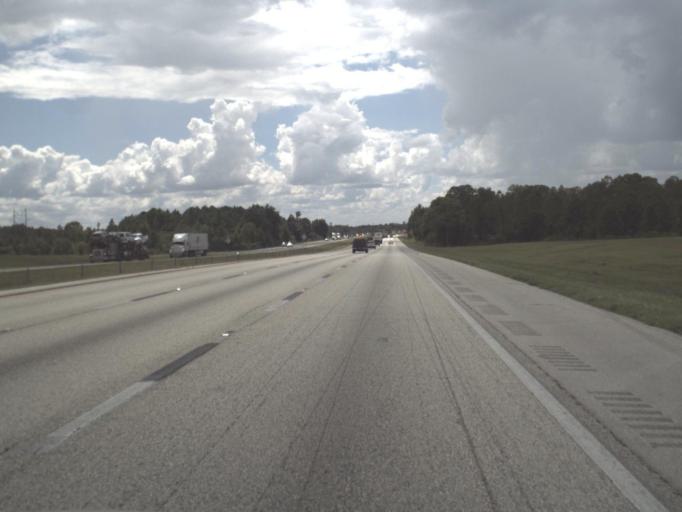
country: US
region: Florida
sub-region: Polk County
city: Davenport
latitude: 28.2032
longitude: -81.6951
